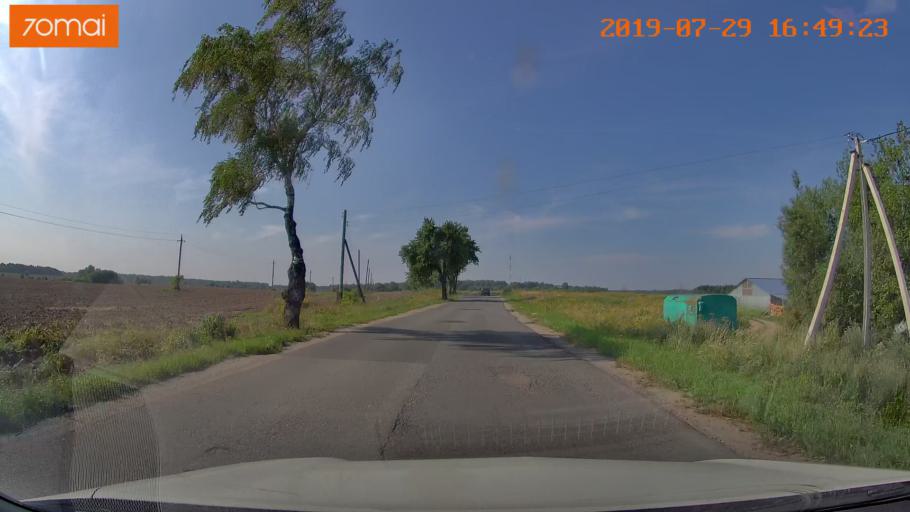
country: RU
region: Kaliningrad
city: Primorsk
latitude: 54.7936
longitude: 20.0659
